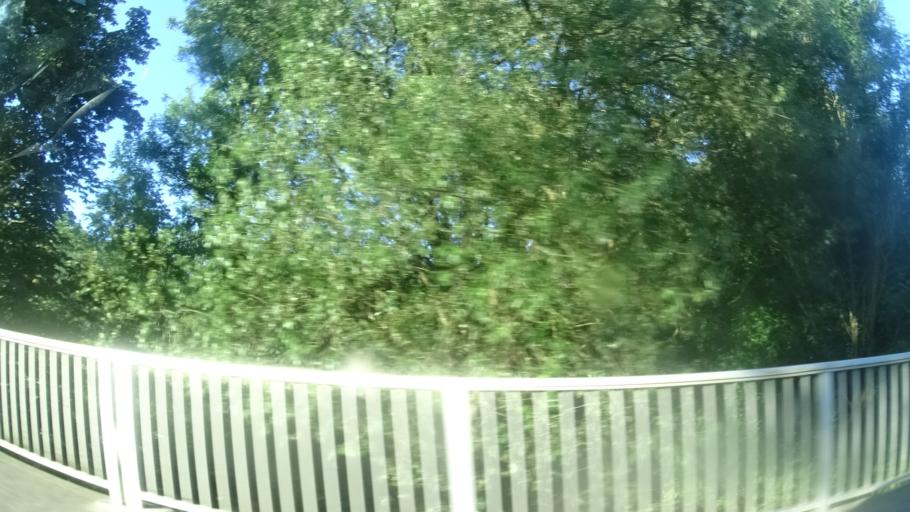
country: DE
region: Lower Saxony
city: Holle
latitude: 52.1019
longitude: 10.1235
